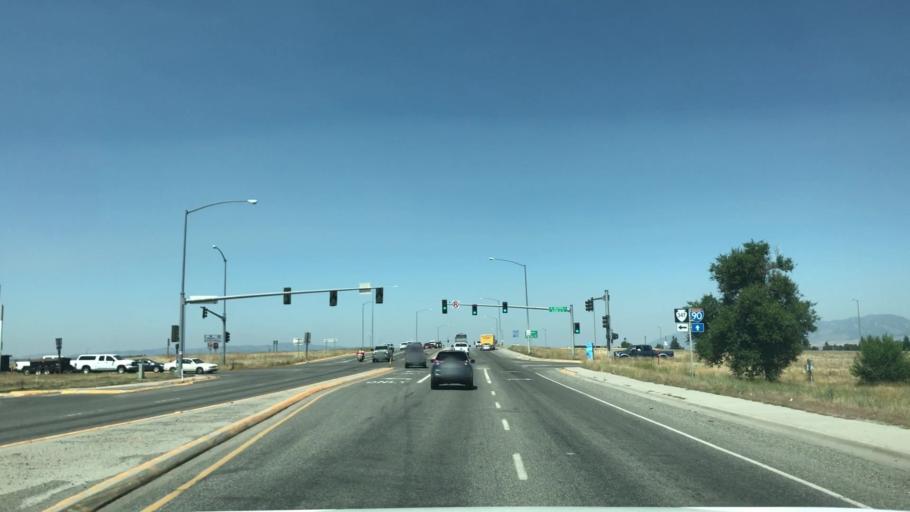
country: US
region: Montana
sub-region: Gallatin County
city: Belgrade
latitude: 45.7651
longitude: -111.1851
